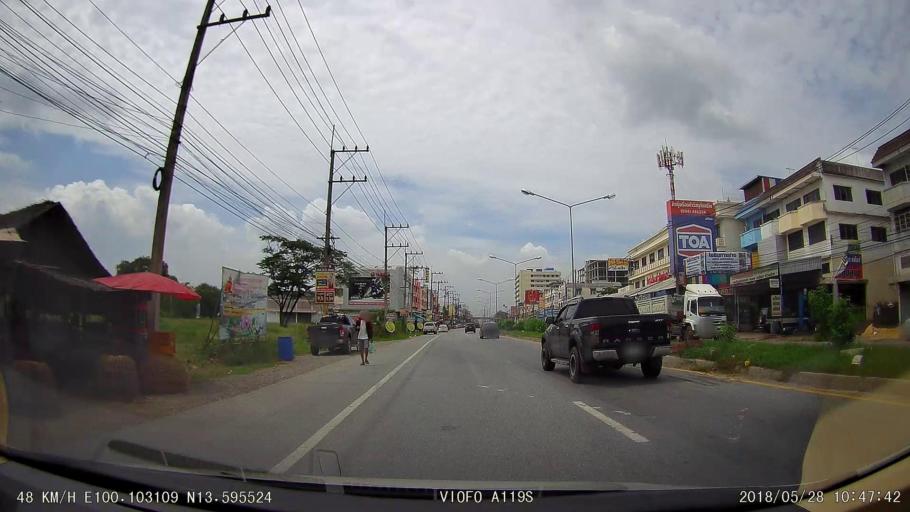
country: TH
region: Samut Sakhon
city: Ban Phaeo
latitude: 13.5954
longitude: 100.1032
